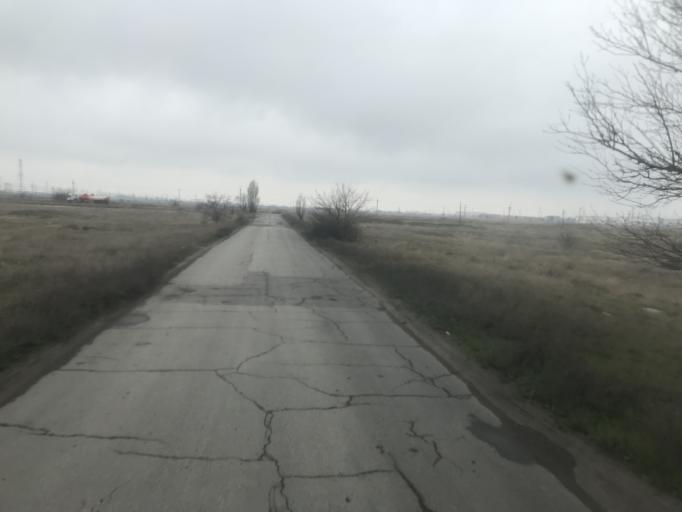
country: RU
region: Volgograd
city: Svetlyy Yar
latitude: 48.5004
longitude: 44.6459
